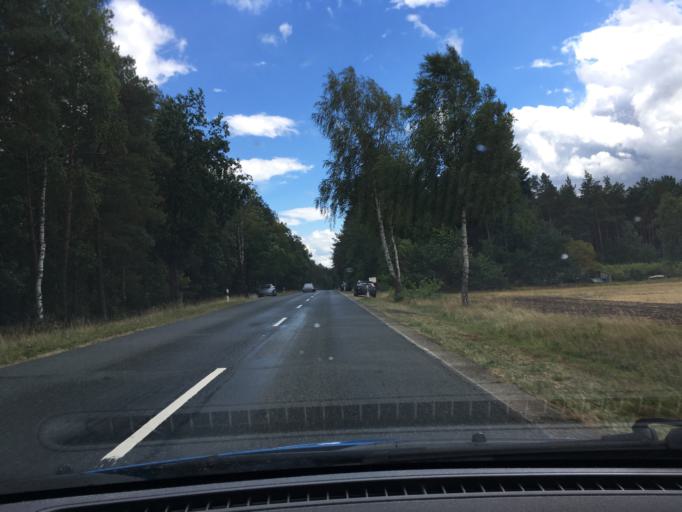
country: DE
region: Lower Saxony
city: Wietzendorf
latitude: 52.9228
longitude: 10.0098
